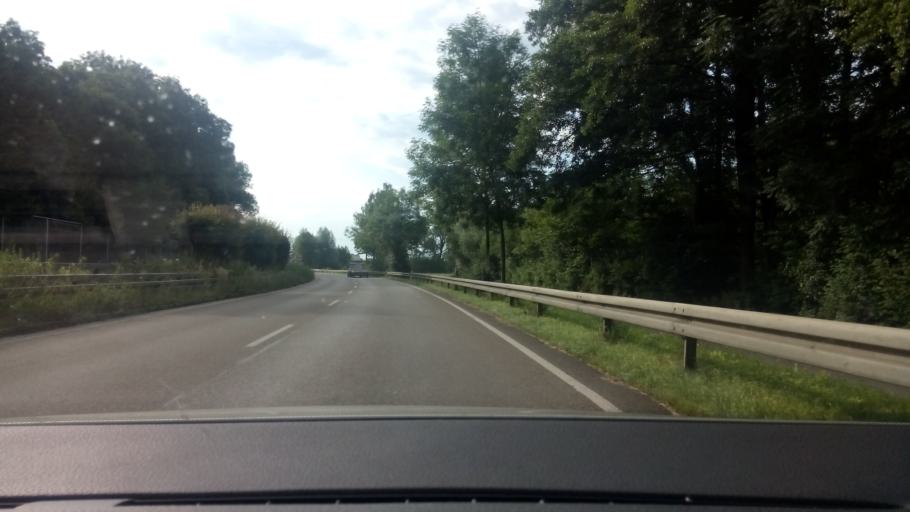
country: DE
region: Bavaria
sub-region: Upper Bavaria
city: Karlsfeld
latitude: 48.2301
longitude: 11.4561
